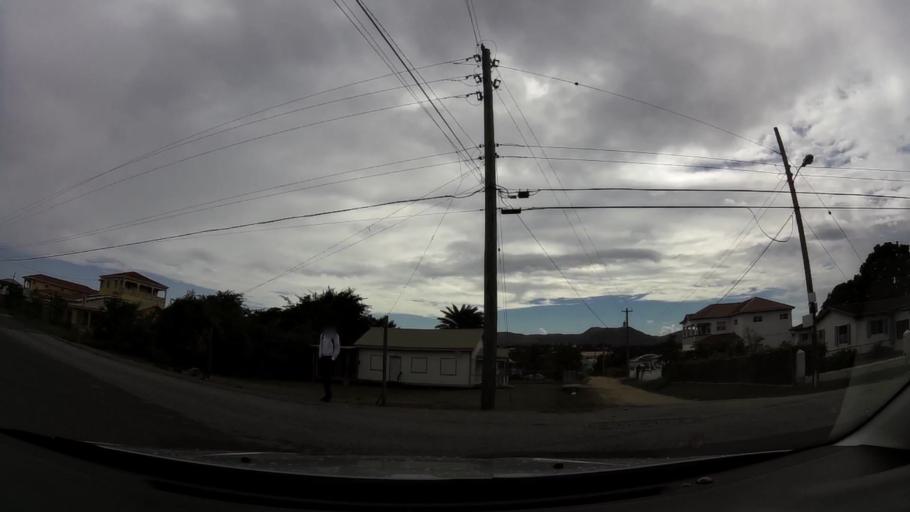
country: AG
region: Saint John
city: Potters Village
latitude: 17.0891
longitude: -61.8136
